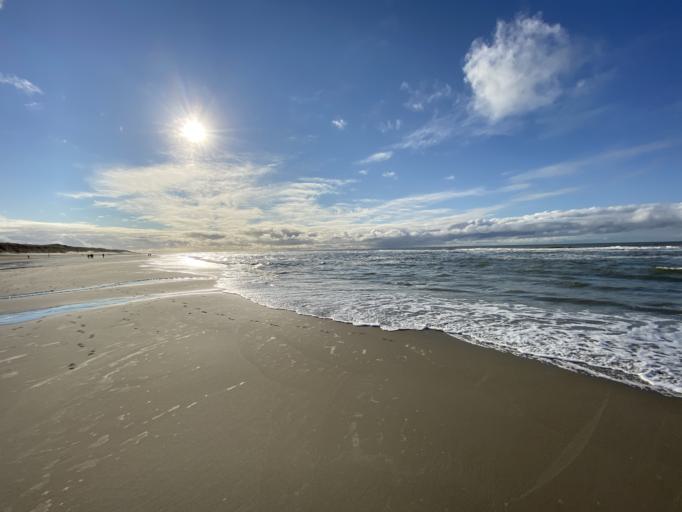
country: NL
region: North Holland
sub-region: Gemeente Texel
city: Den Burg
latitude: 53.0975
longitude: 4.7489
